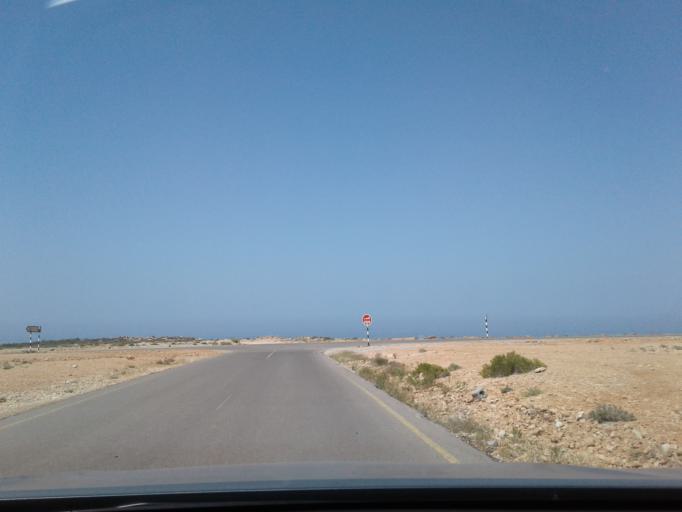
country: OM
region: Ash Sharqiyah
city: Al Qabil
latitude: 23.0409
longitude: 59.0727
